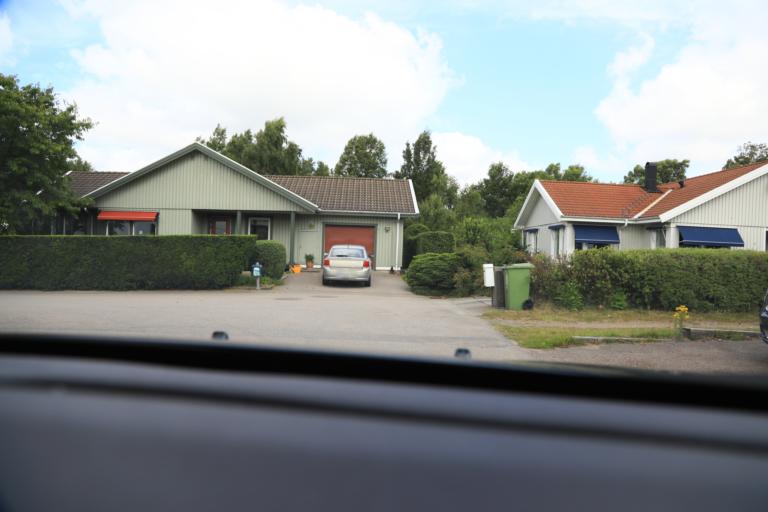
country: SE
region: Halland
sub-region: Varbergs Kommun
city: Varberg
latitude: 57.1139
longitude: 12.2944
